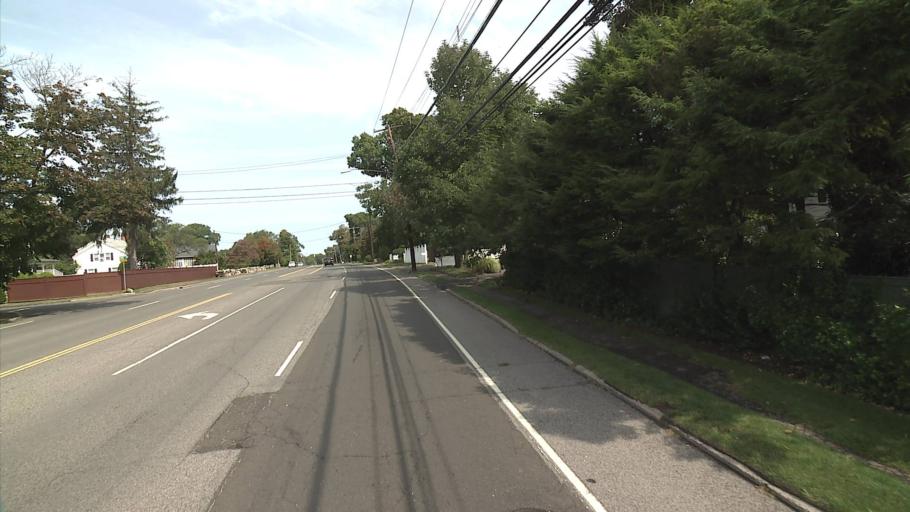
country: US
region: Connecticut
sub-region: Fairfield County
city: Stamford
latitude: 41.0905
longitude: -73.5479
